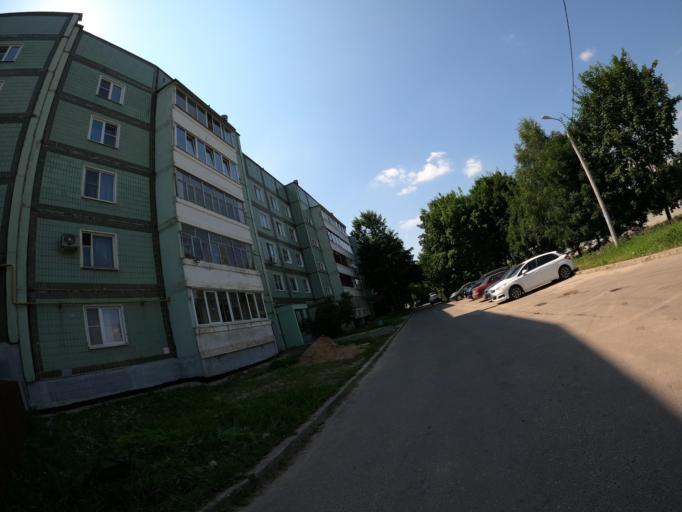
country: RU
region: Kaluga
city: Obninsk
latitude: 55.1222
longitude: 36.5882
